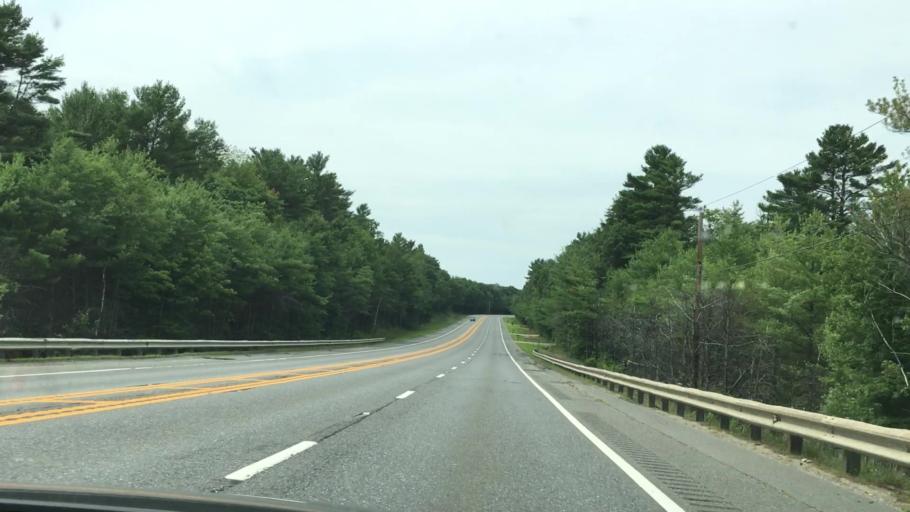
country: US
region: Massachusetts
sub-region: Worcester County
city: Gardner
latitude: 42.6141
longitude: -72.0030
